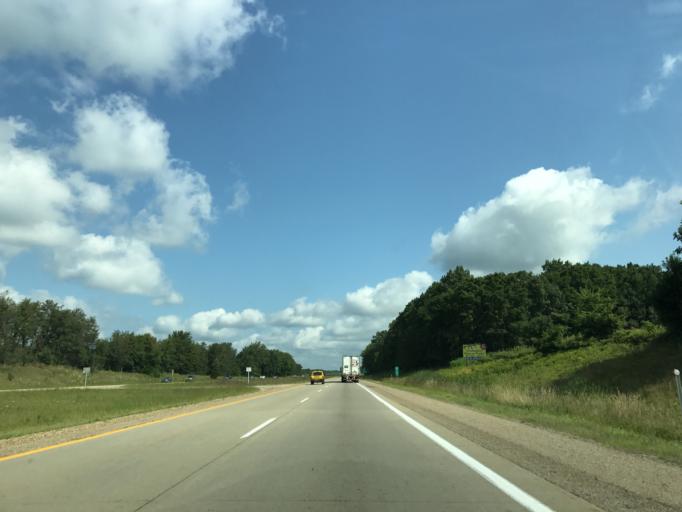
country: US
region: Michigan
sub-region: Branch County
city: Coldwater
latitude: 41.8868
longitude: -84.9906
